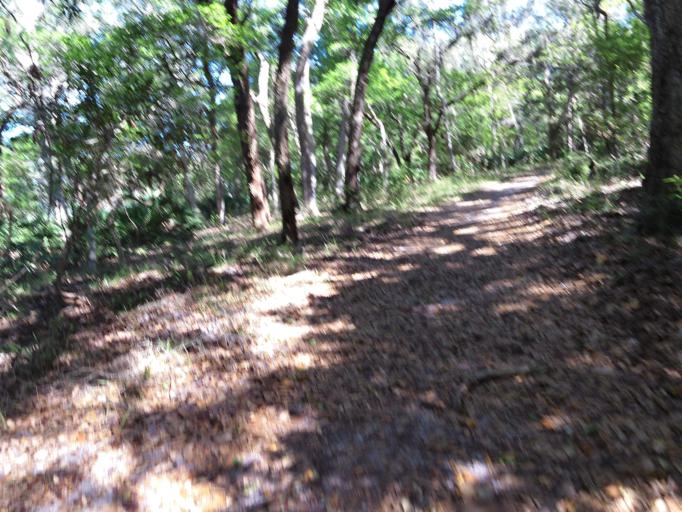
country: US
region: Florida
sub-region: Saint Johns County
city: Villano Beach
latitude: 29.9982
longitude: -81.3277
